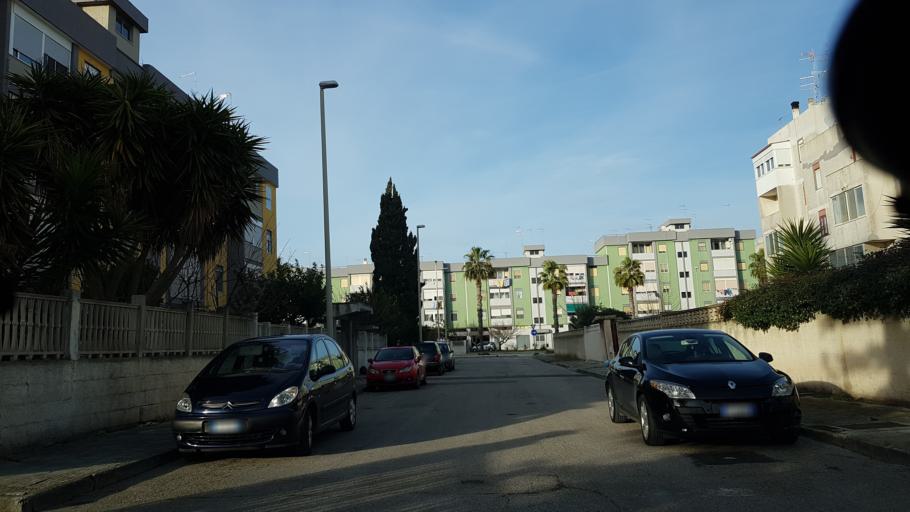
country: IT
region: Apulia
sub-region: Provincia di Brindisi
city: Brindisi
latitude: 40.6161
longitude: 17.9273
